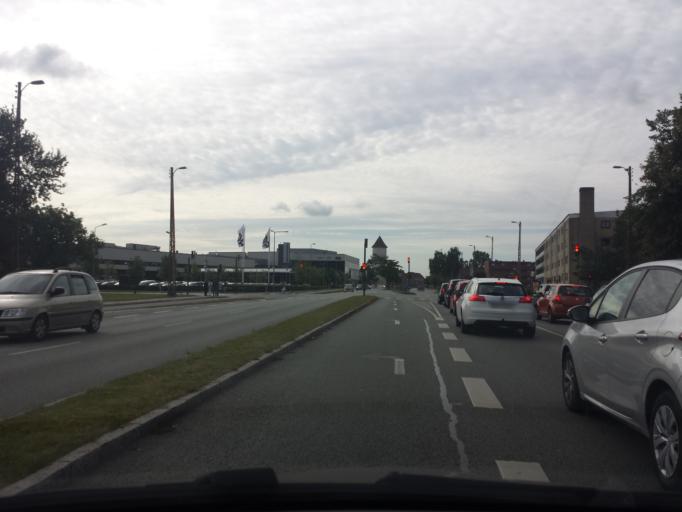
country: DK
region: Capital Region
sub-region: Rodovre Kommune
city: Rodovre
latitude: 55.6812
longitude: 12.4532
